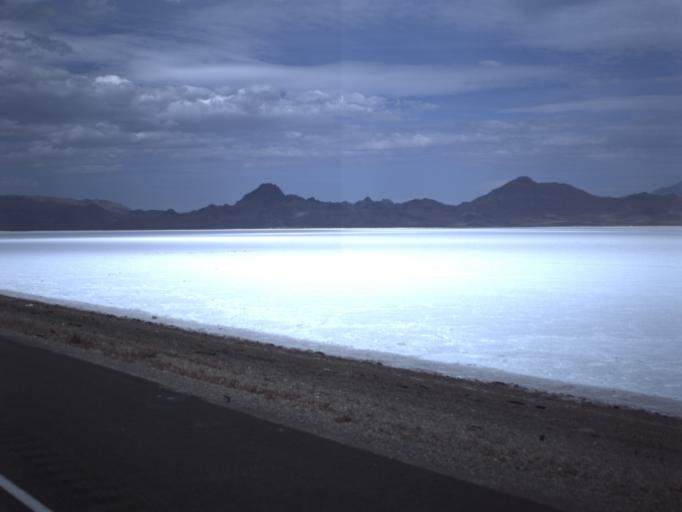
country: US
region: Utah
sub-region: Tooele County
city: Wendover
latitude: 40.7398
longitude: -113.8703
